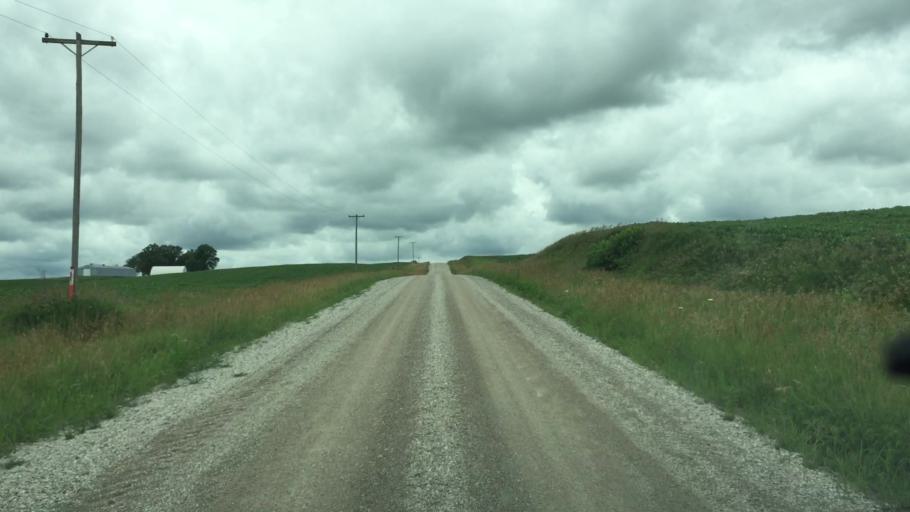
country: US
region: Iowa
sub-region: Jasper County
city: Monroe
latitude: 41.6010
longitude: -93.1285
